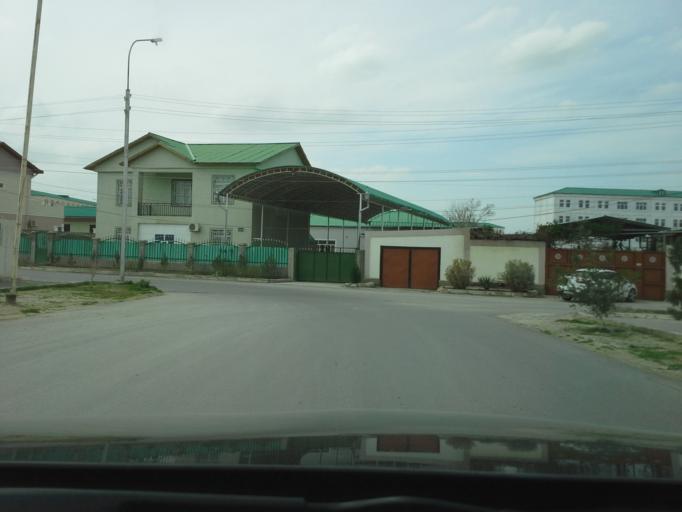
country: TM
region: Ahal
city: Abadan
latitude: 38.0596
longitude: 58.1427
